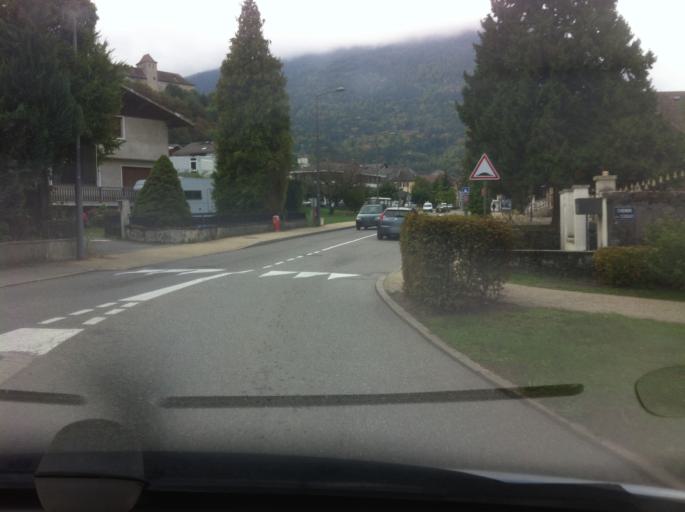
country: FR
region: Rhone-Alpes
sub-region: Departement de la Haute-Savoie
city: Faverges
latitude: 45.7484
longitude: 6.2987
